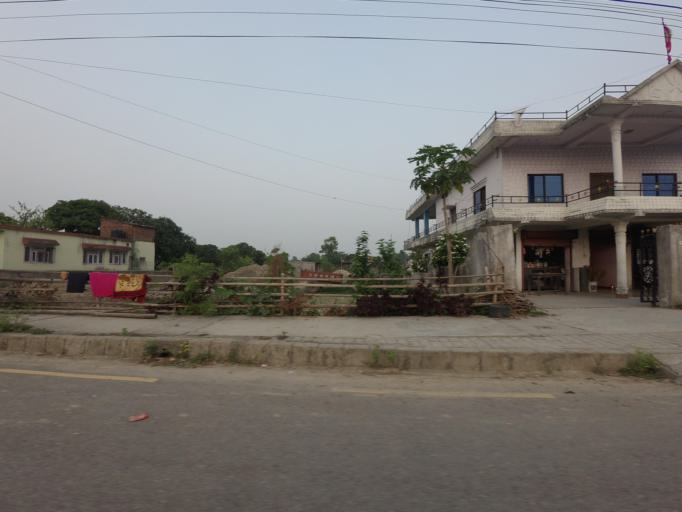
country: NP
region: Western Region
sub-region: Lumbini Zone
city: Bhairahawa
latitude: 27.5023
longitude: 83.4637
